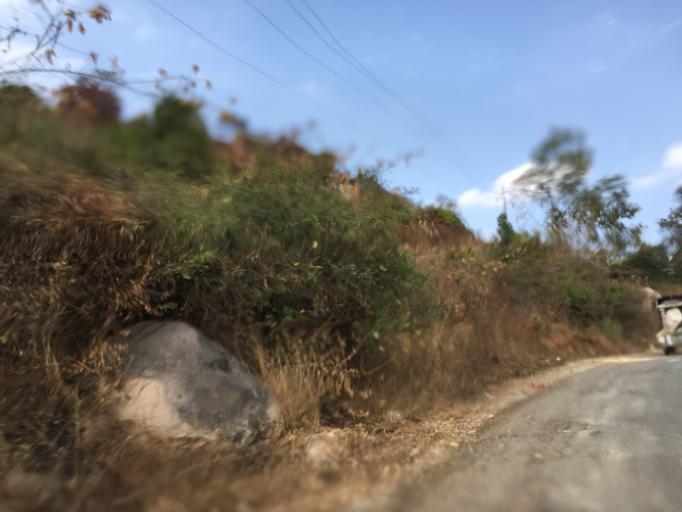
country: IN
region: Karnataka
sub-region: Chikkaballapur
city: Chik Ballapur
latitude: 13.3757
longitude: 77.6689
